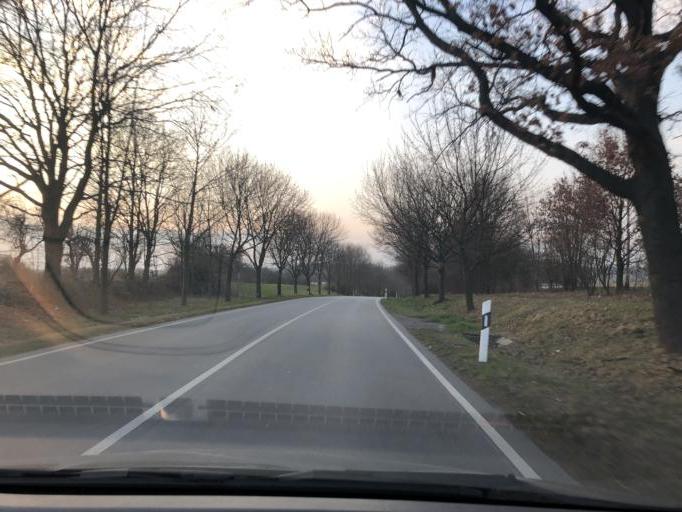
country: DE
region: Saxony
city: Goda
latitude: 51.2014
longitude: 14.3131
